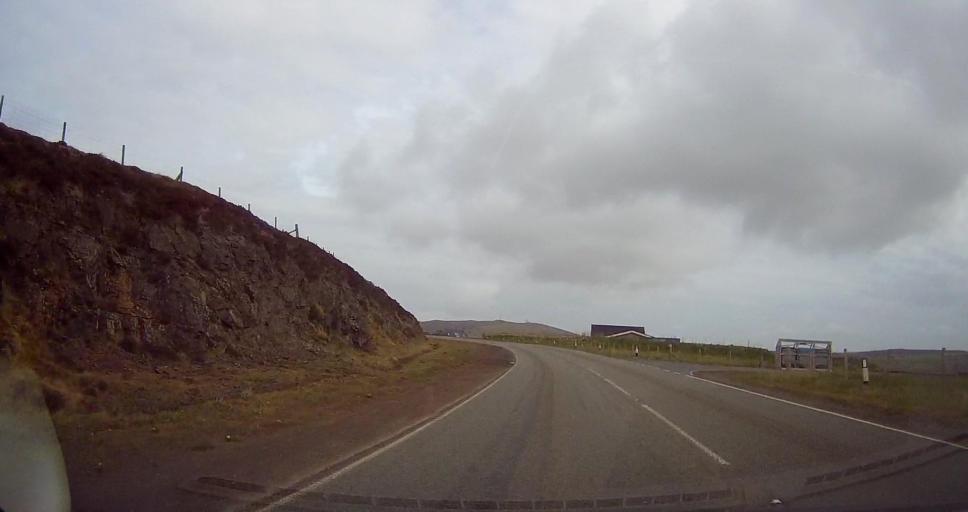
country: GB
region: Scotland
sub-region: Shetland Islands
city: Lerwick
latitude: 60.1188
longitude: -1.2157
